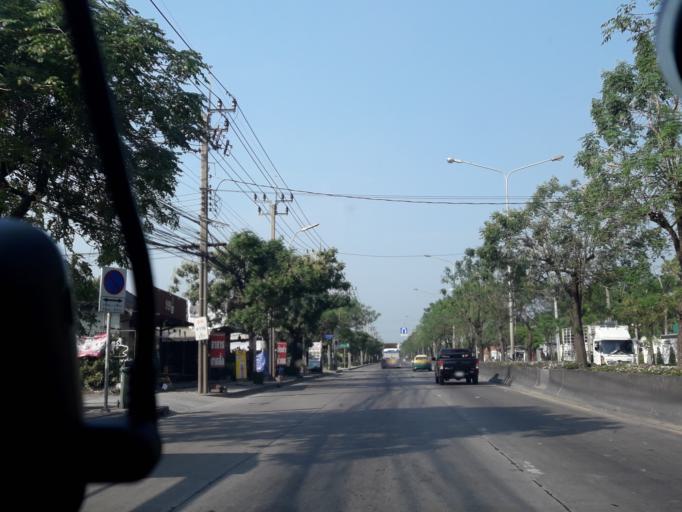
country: TH
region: Bangkok
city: Khlong Sam Wa
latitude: 13.8686
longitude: 100.7318
